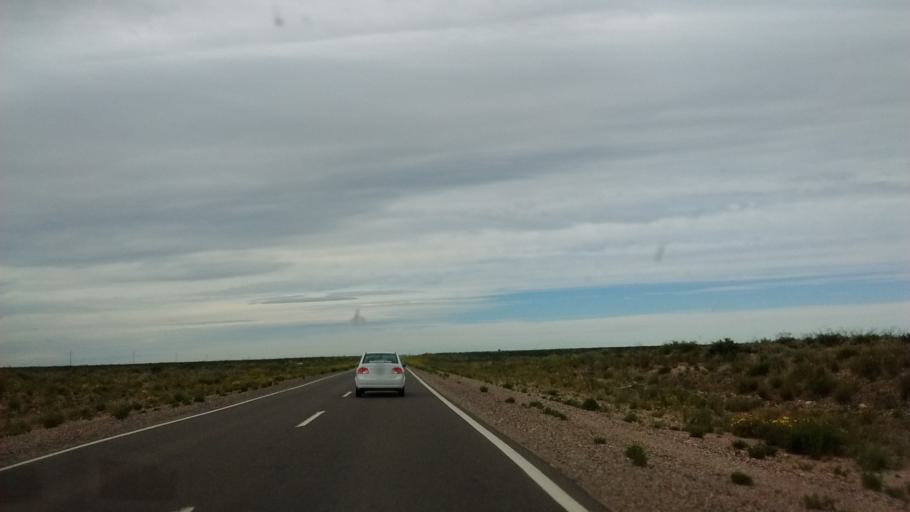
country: AR
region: Rio Negro
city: Contraalmirante Cordero
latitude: -38.3350
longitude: -68.0097
